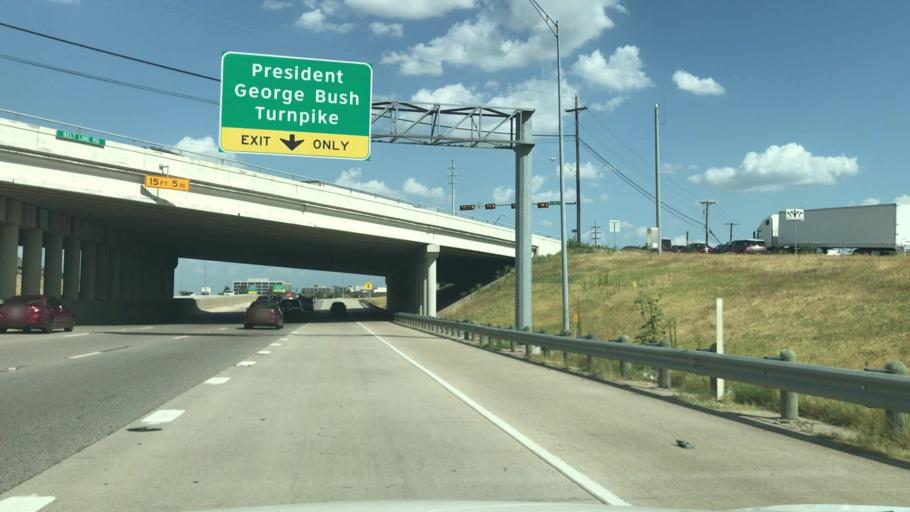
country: US
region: Texas
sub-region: Dallas County
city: Coppell
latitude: 32.9058
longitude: -96.9932
